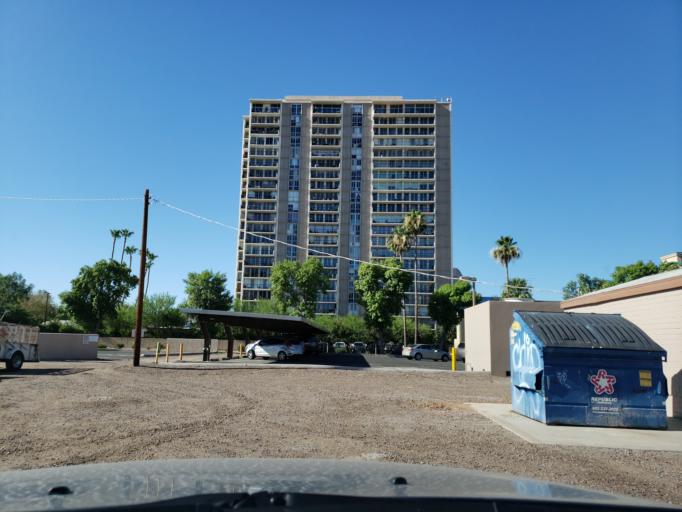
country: US
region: Arizona
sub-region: Maricopa County
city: Phoenix
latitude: 33.4750
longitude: -112.0732
